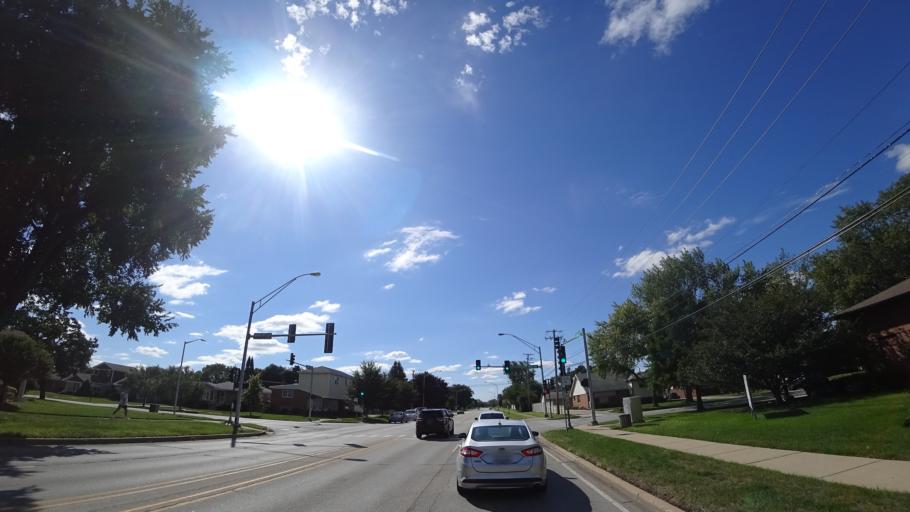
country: US
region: Illinois
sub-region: Cook County
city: Oak Lawn
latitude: 41.7055
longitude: -87.7496
